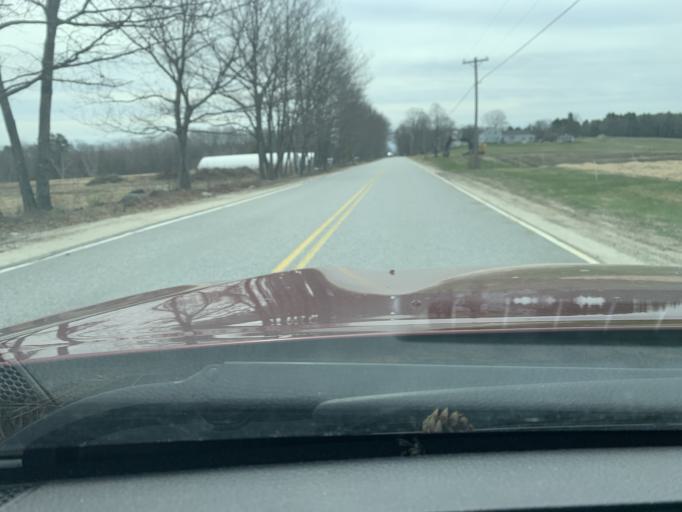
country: US
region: Maine
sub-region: Cumberland County
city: Raymond
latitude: 43.9592
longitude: -70.3895
